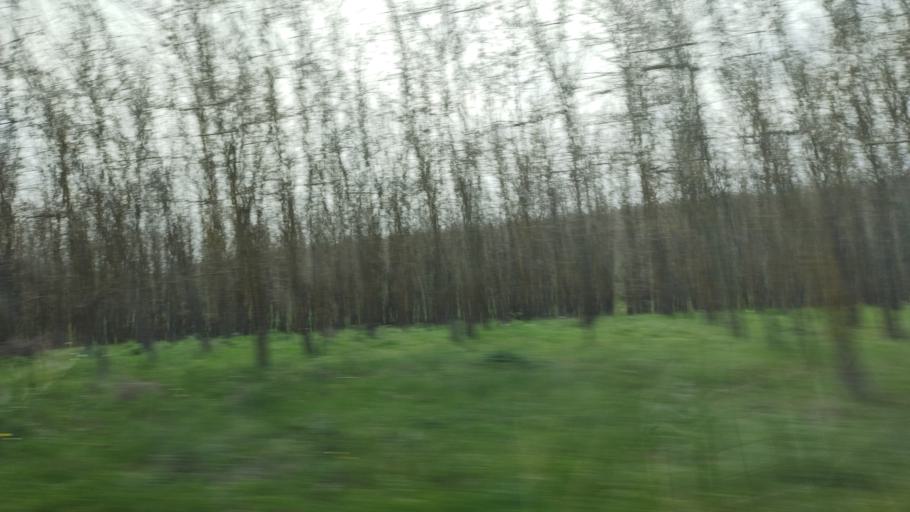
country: RO
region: Constanta
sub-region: Comuna Deleni
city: Pietreni
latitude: 44.0897
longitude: 28.0866
